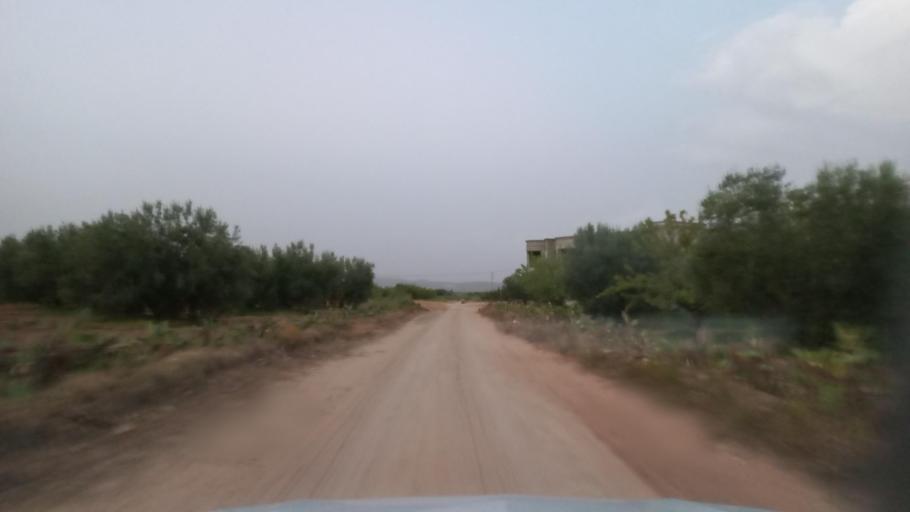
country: TN
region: Al Qasrayn
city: Kasserine
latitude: 35.2782
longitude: 9.0332
